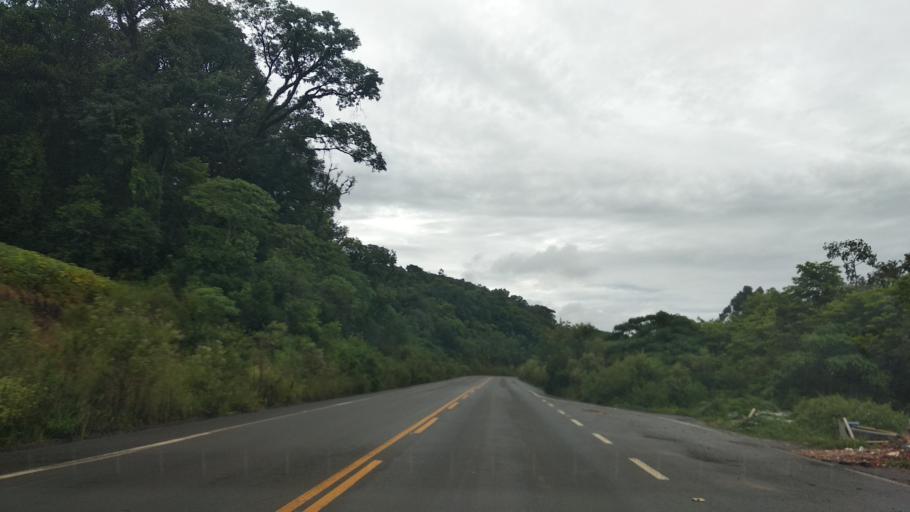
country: BR
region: Santa Catarina
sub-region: Videira
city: Videira
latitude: -27.0109
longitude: -51.1698
